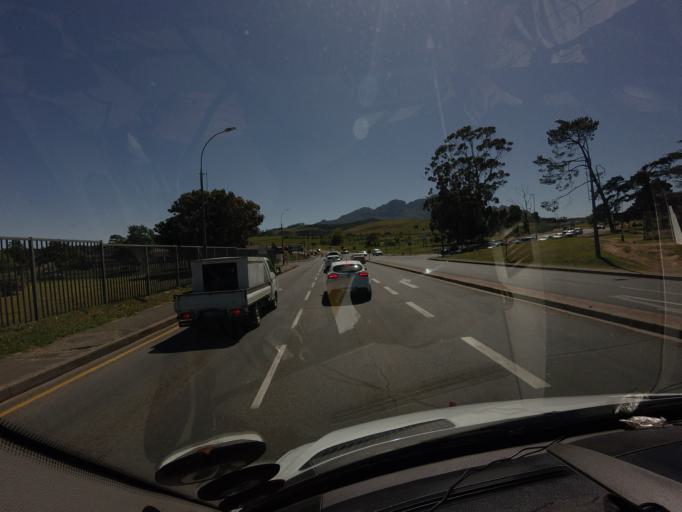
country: ZA
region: Western Cape
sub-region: Cape Winelands District Municipality
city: Stellenbosch
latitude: -33.9228
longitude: 18.8576
